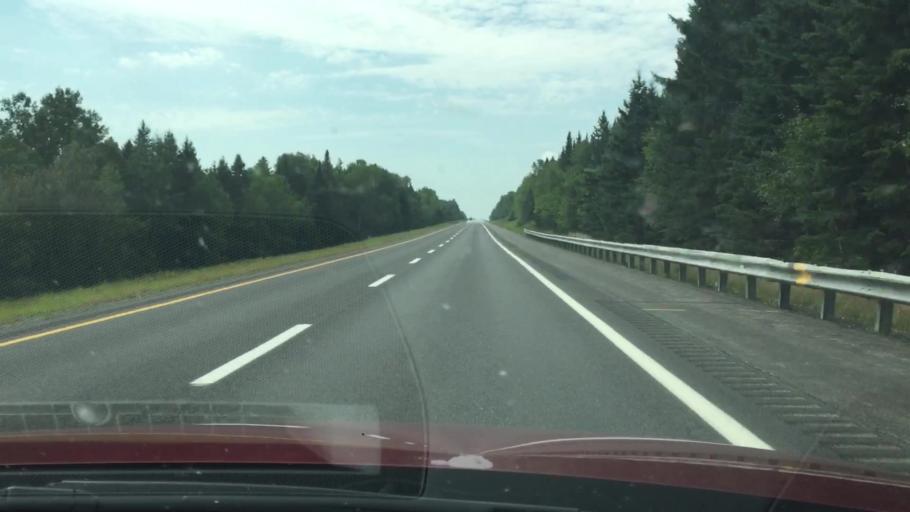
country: US
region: Maine
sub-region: Aroostook County
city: Hodgdon
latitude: 46.1300
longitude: -68.0959
